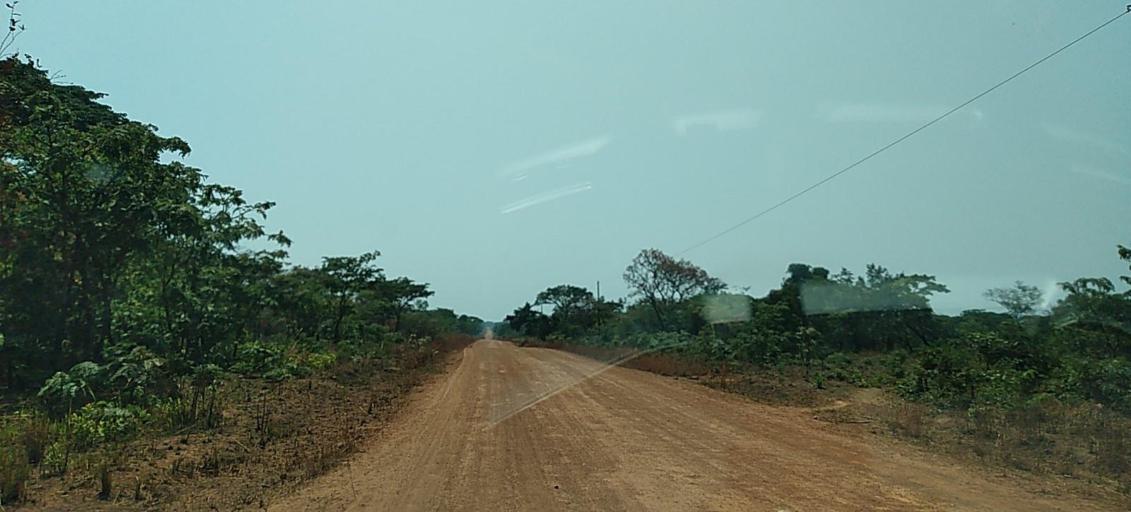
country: ZM
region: North-Western
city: Kansanshi
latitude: -11.9926
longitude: 26.6234
